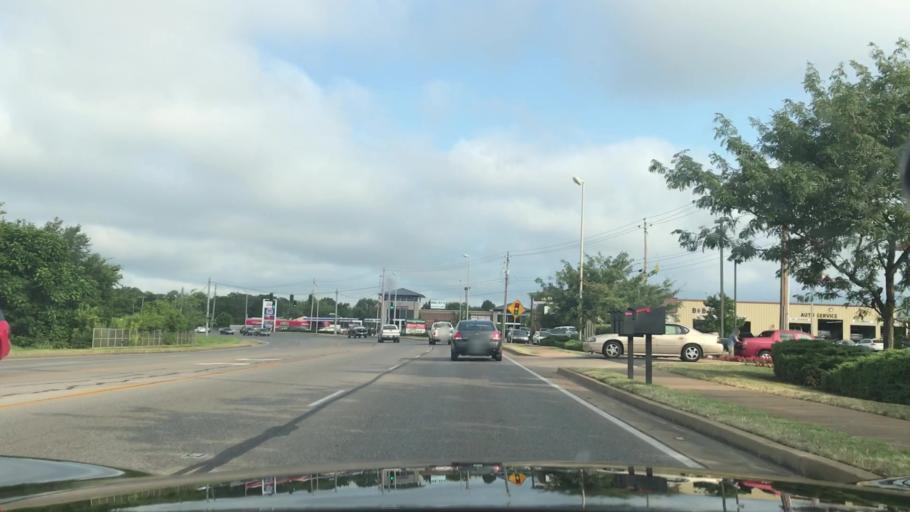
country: US
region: Kentucky
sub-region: Warren County
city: Bowling Green
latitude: 36.9594
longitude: -86.4502
